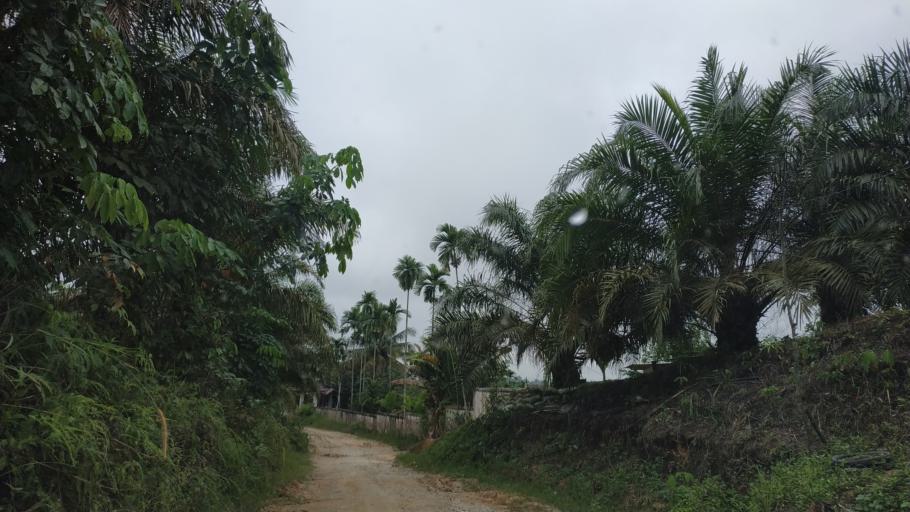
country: ID
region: Riau
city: Pekanbaru
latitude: 0.4825
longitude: 101.5613
